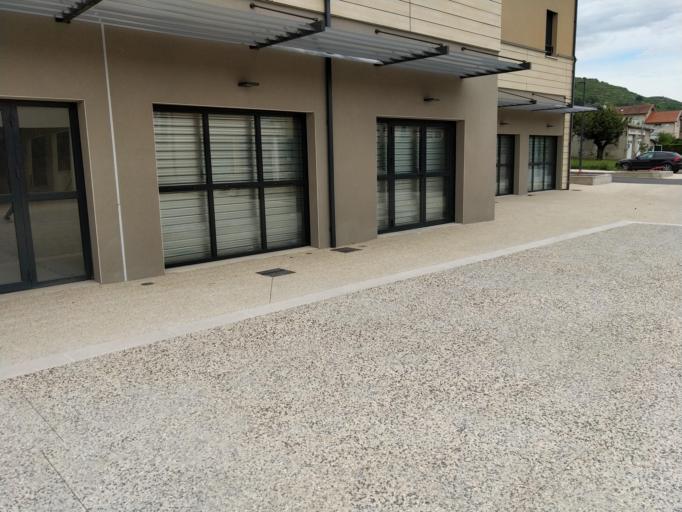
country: FR
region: Rhone-Alpes
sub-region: Departement de l'Ardeche
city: Andance
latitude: 45.2542
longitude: 4.7834
